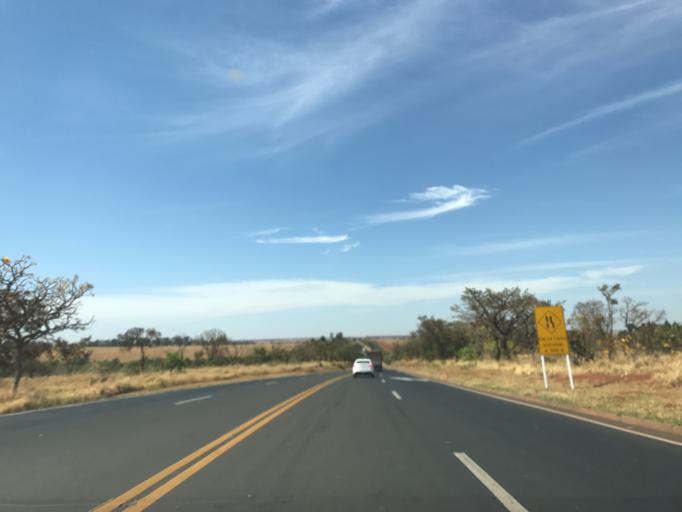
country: BR
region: Minas Gerais
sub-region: Monte Alegre De Minas
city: Monte Alegre de Minas
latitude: -18.8982
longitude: -49.0434
